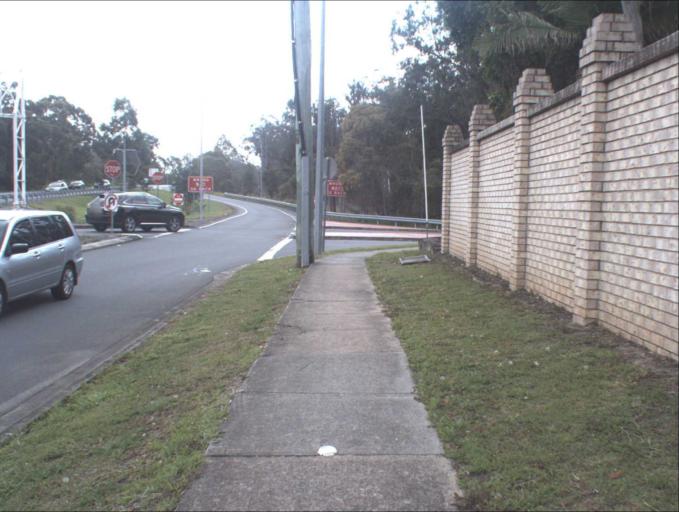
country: AU
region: Queensland
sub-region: Brisbane
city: Sunnybank Hills
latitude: -27.6543
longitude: 153.0407
